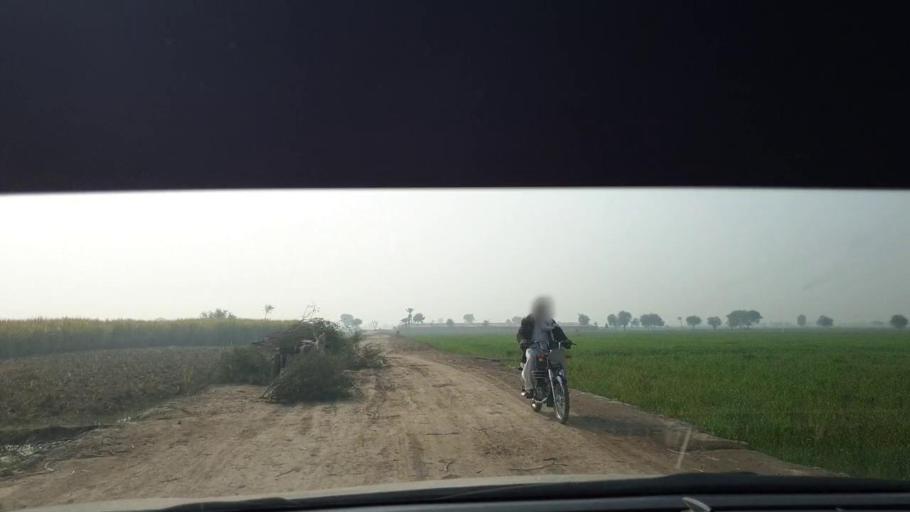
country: PK
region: Sindh
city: Berani
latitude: 25.7834
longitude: 68.7977
